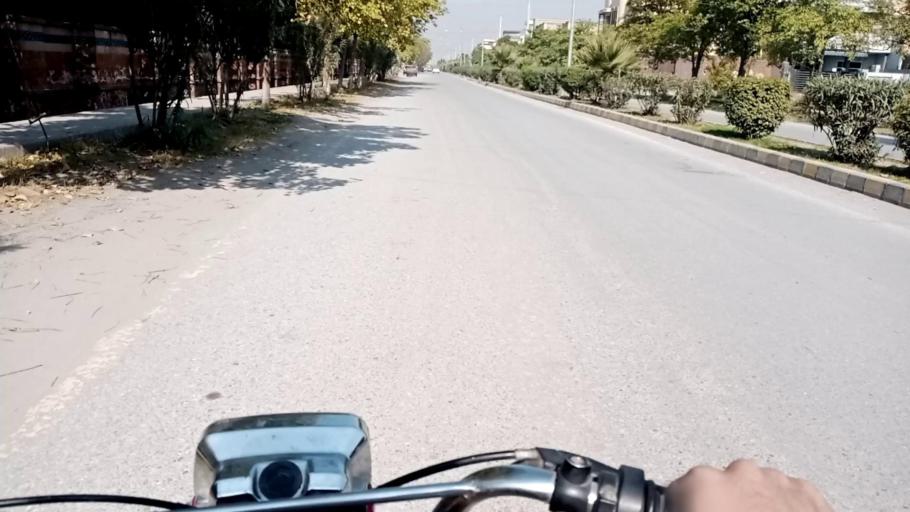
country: PK
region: Khyber Pakhtunkhwa
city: Peshawar
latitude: 33.9582
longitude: 71.4176
